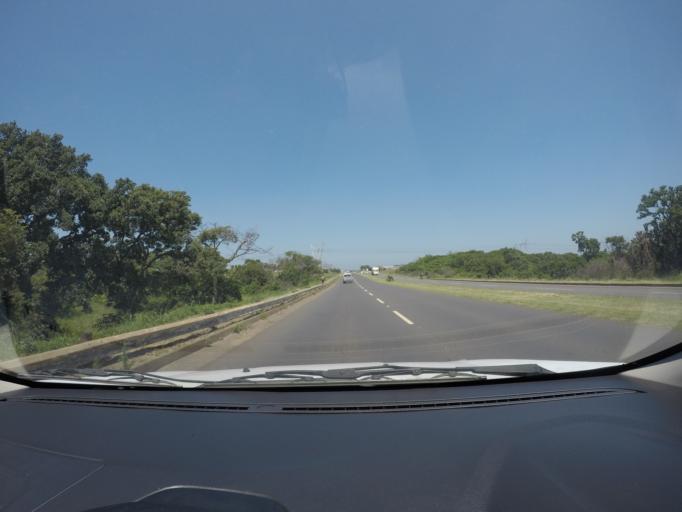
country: ZA
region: KwaZulu-Natal
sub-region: uThungulu District Municipality
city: Richards Bay
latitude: -28.7552
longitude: 32.0393
